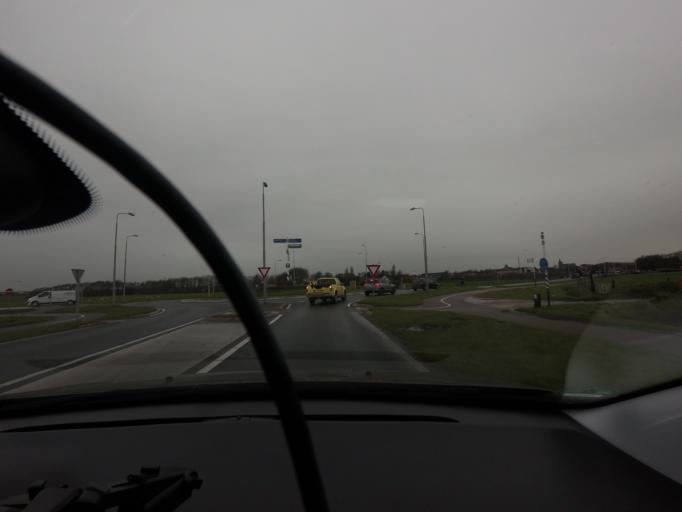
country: NL
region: North Holland
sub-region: Gemeente Texel
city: Den Burg
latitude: 53.0474
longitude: 4.7930
